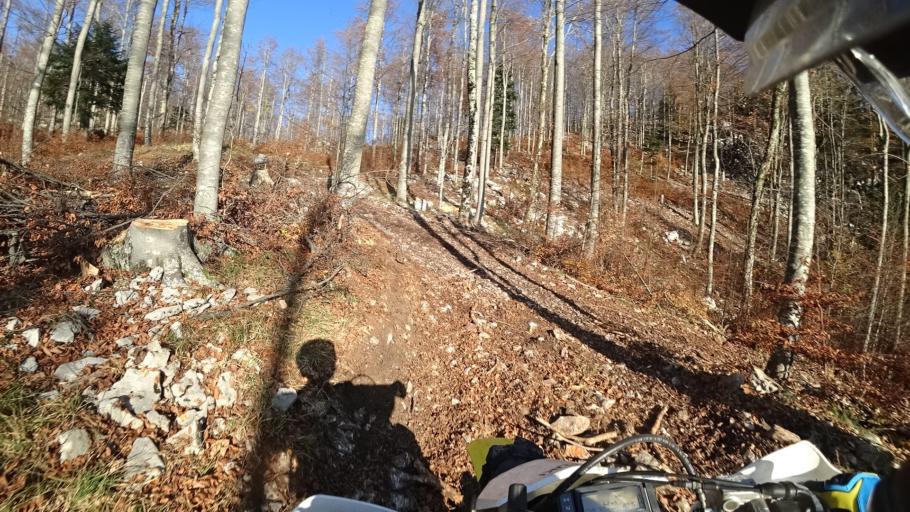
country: HR
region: Primorsko-Goranska
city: Klana
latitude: 45.4796
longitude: 14.4428
